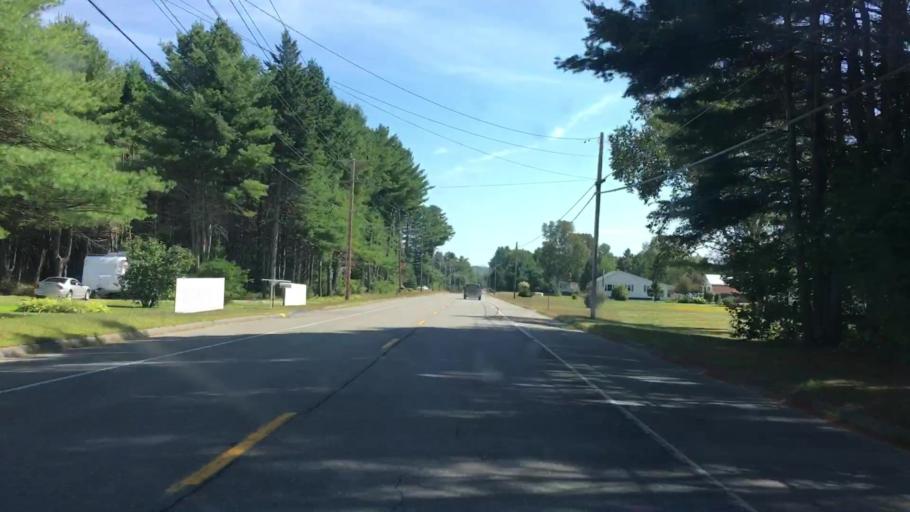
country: US
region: Maine
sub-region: Piscataquis County
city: Milo
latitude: 45.2400
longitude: -68.9685
